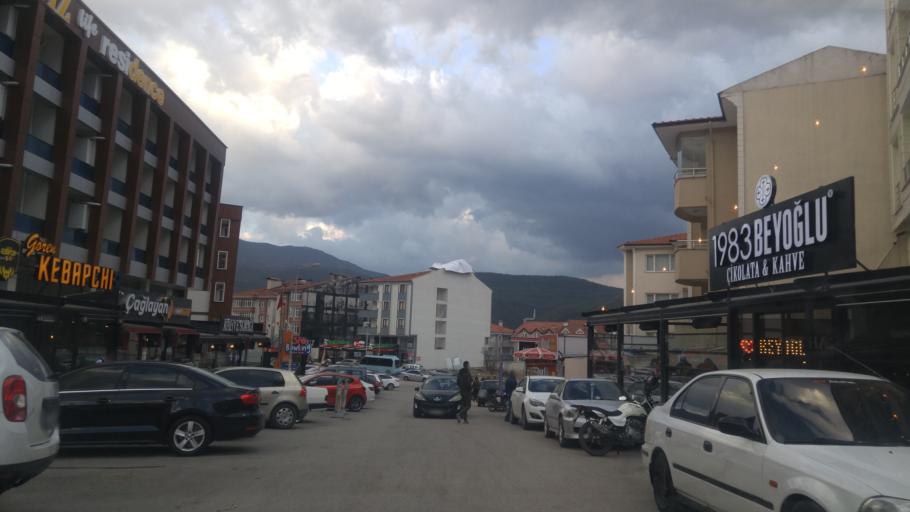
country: TR
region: Karabuk
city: Safranbolu
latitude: 41.2192
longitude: 32.6669
